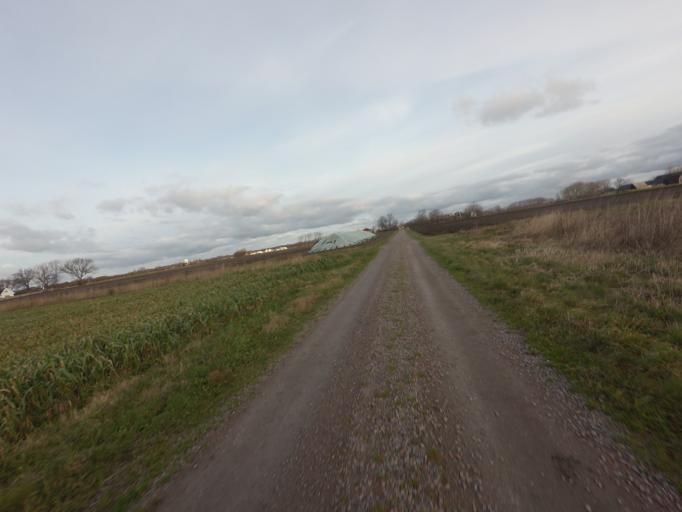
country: SE
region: Skane
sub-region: Hoganas Kommun
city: Hoganas
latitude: 56.1661
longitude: 12.5799
